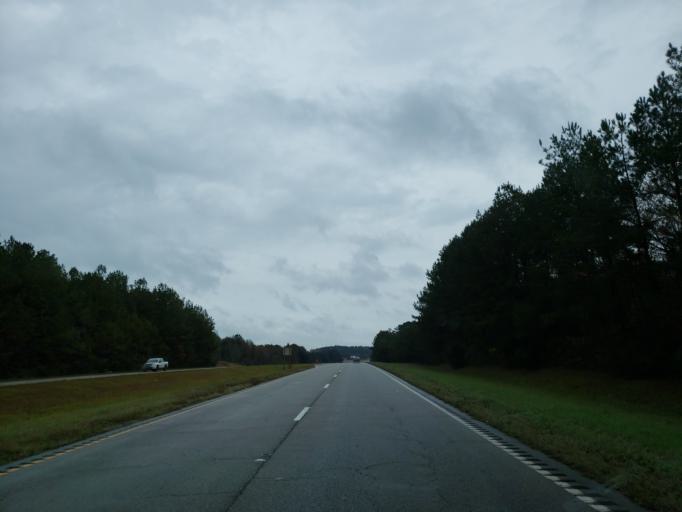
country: US
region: Mississippi
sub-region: Jones County
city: Laurel
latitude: 31.7037
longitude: -89.0805
